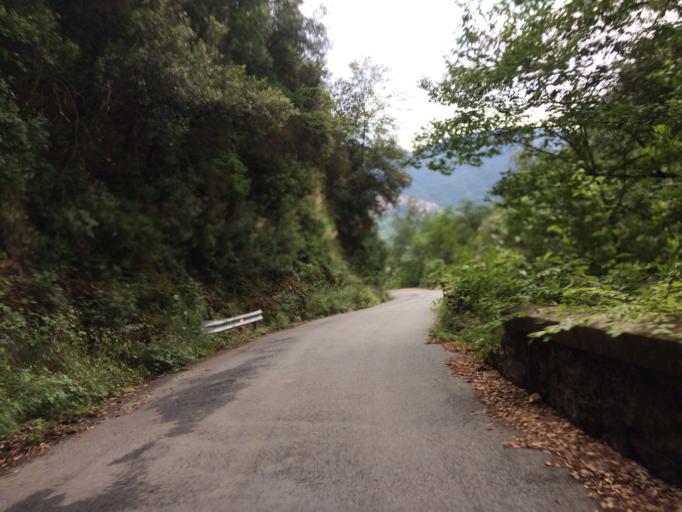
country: IT
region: Liguria
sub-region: Provincia di Imperia
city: Castel Vittorio
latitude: 43.9414
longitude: 7.6855
